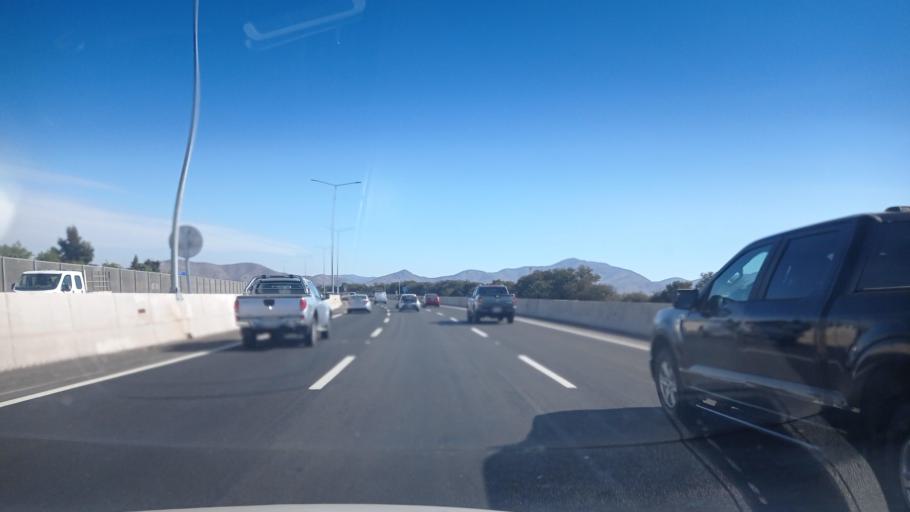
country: CL
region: Santiago Metropolitan
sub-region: Provincia de Santiago
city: Lo Prado
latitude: -33.4986
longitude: -70.7940
